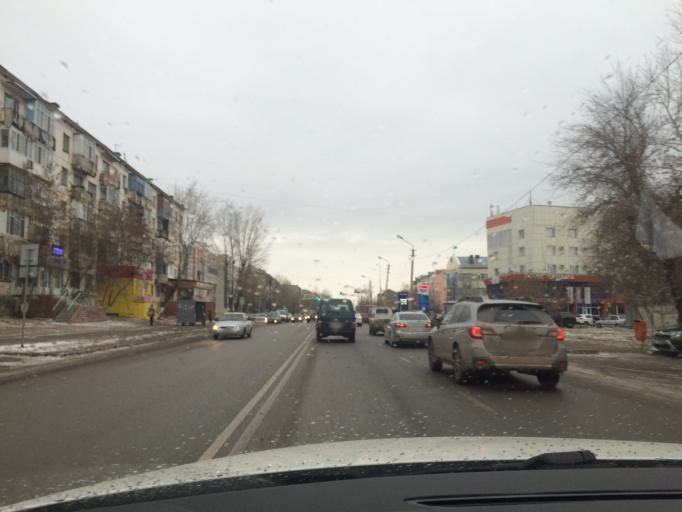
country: KZ
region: Astana Qalasy
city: Astana
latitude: 51.1851
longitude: 71.4217
